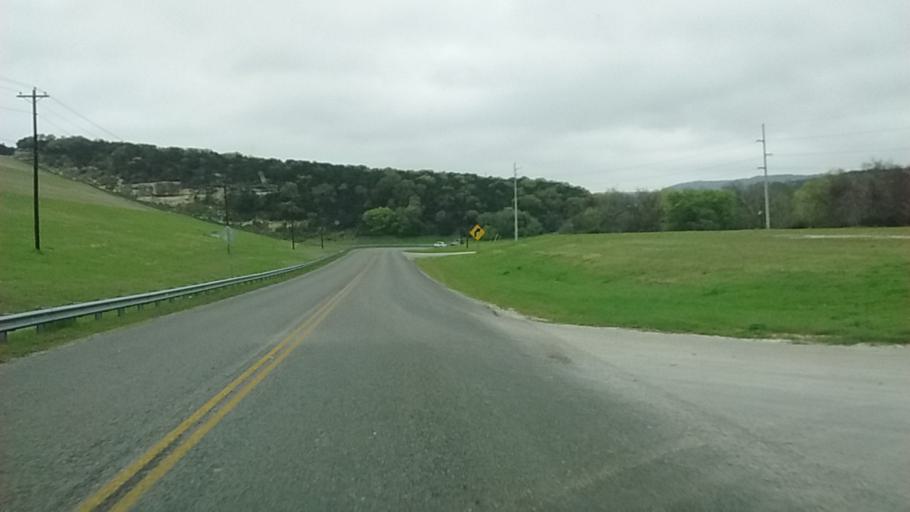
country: US
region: Texas
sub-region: Comal County
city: Canyon Lake
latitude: 29.8703
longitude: -98.1961
